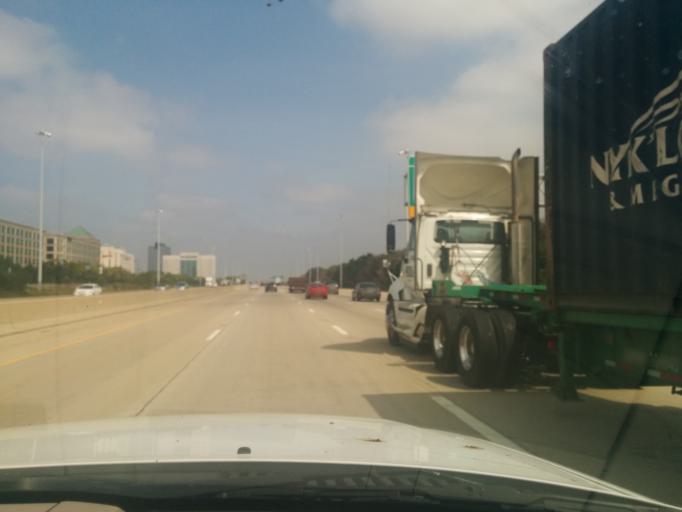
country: US
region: Illinois
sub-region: Cook County
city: Hoffman Estates
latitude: 42.0235
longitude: -88.0310
